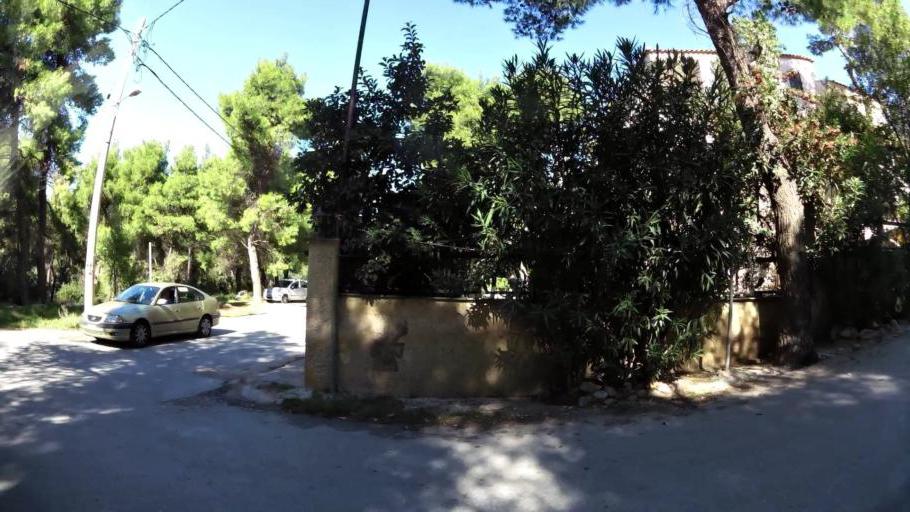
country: GR
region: Attica
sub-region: Nomarchia Anatolikis Attikis
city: Drosia
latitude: 38.1127
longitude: 23.8719
